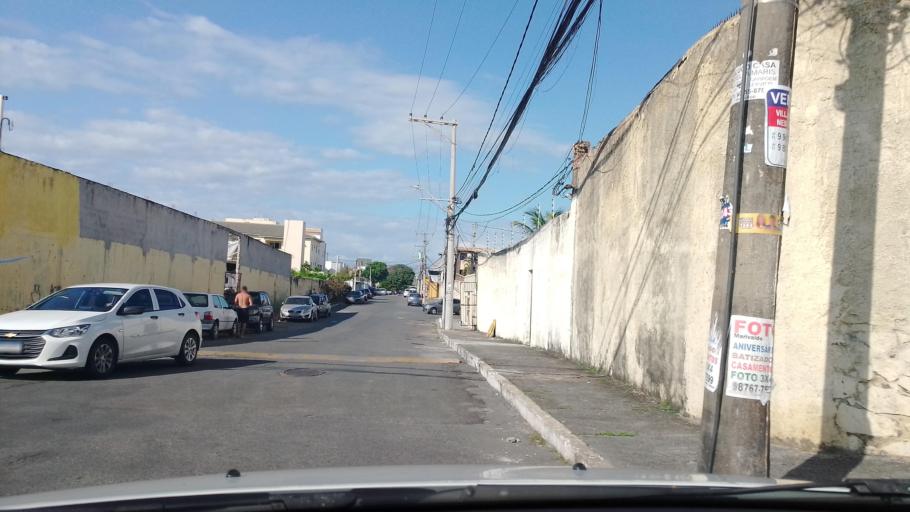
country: BR
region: Bahia
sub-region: Lauro De Freitas
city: Lauro de Freitas
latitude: -12.9370
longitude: -38.3304
